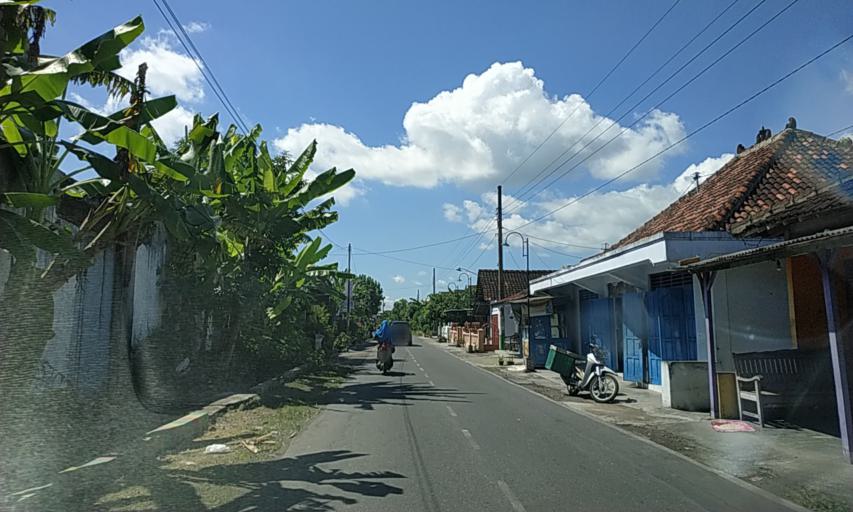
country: ID
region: Central Java
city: Trucuk
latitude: -7.7318
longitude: 110.7028
